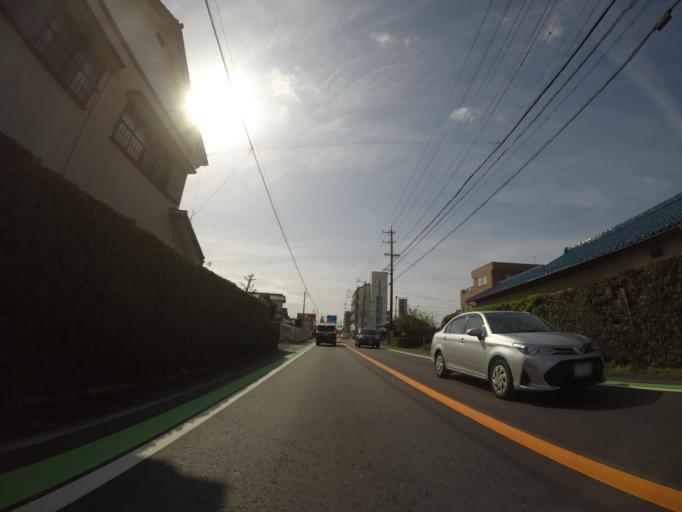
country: JP
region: Shizuoka
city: Hamakita
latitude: 34.7815
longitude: 137.7094
